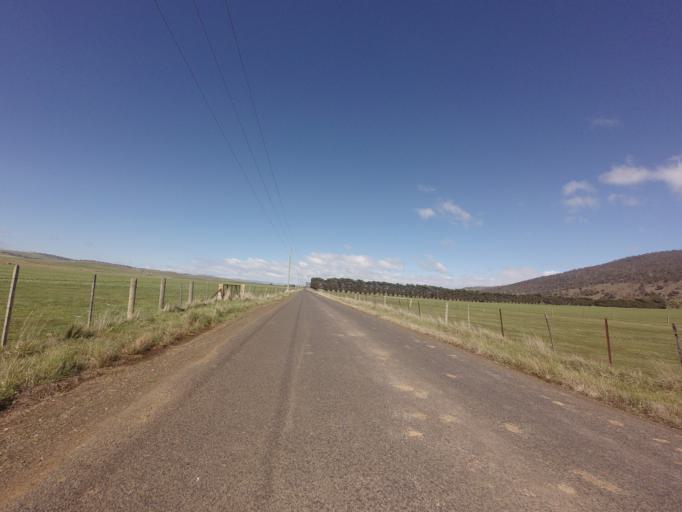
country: AU
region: Tasmania
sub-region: Northern Midlands
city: Evandale
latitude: -41.9641
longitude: 147.4400
